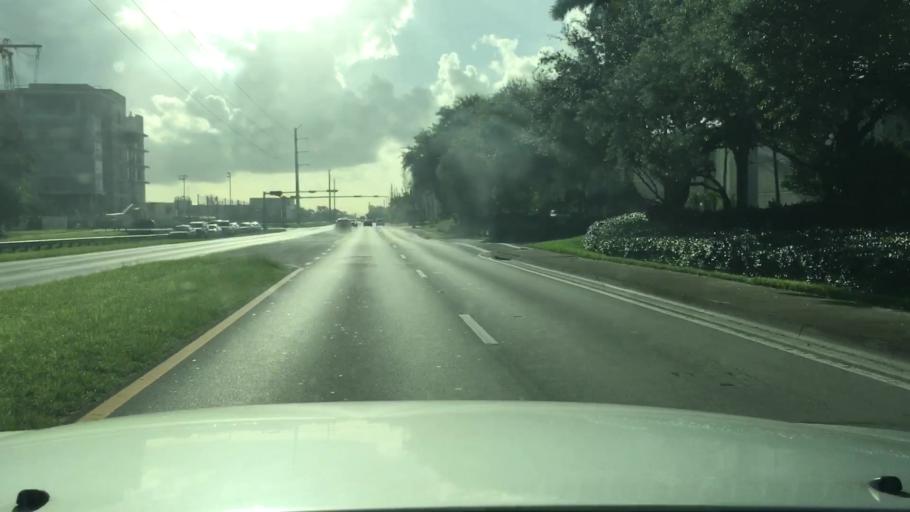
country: US
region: Florida
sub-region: Miami-Dade County
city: Doral
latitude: 25.7967
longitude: -80.3787
